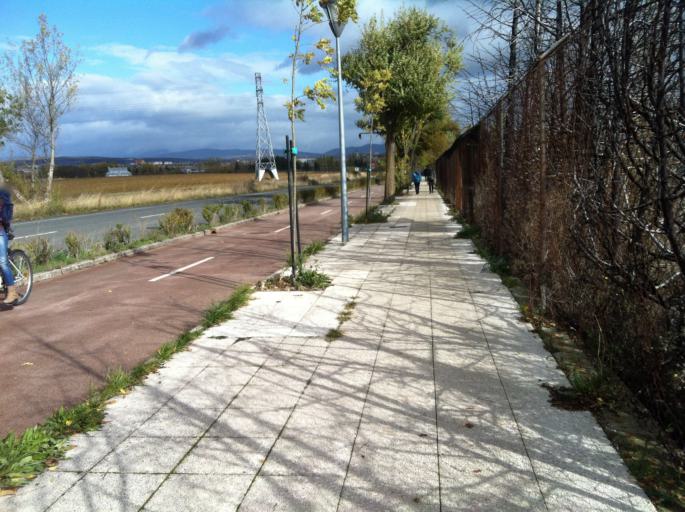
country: ES
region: Basque Country
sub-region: Provincia de Alava
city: Gasteiz / Vitoria
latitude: 42.8275
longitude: -2.6935
